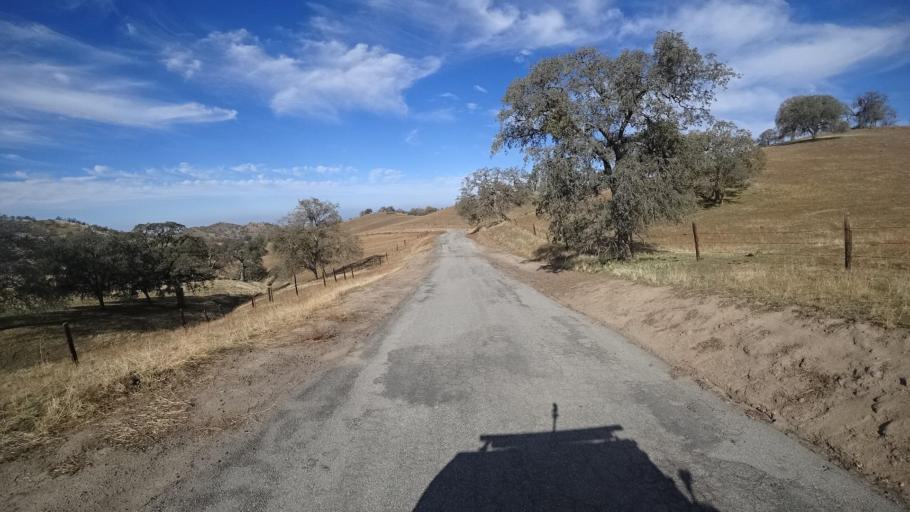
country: US
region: California
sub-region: Kern County
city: Oildale
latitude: 35.5715
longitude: -118.8002
